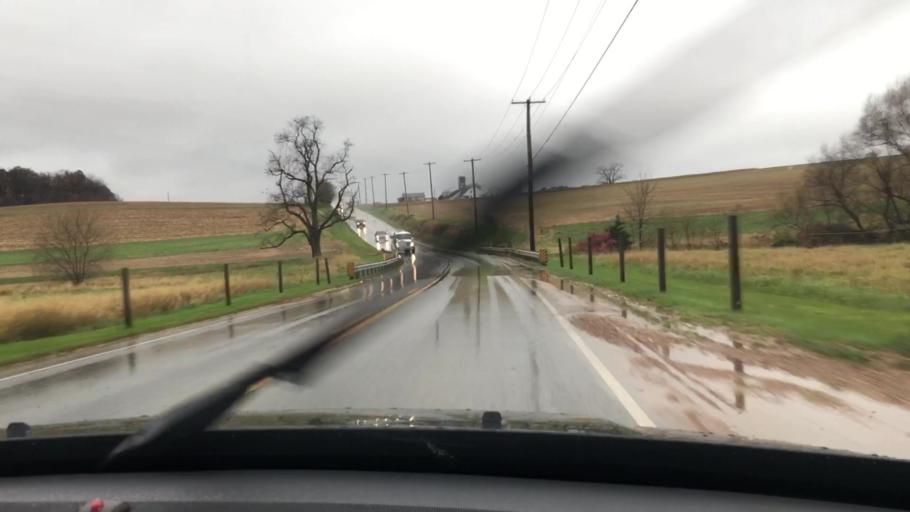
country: US
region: Pennsylvania
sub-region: Lancaster County
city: Quarryville
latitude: 39.8716
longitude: -76.2391
